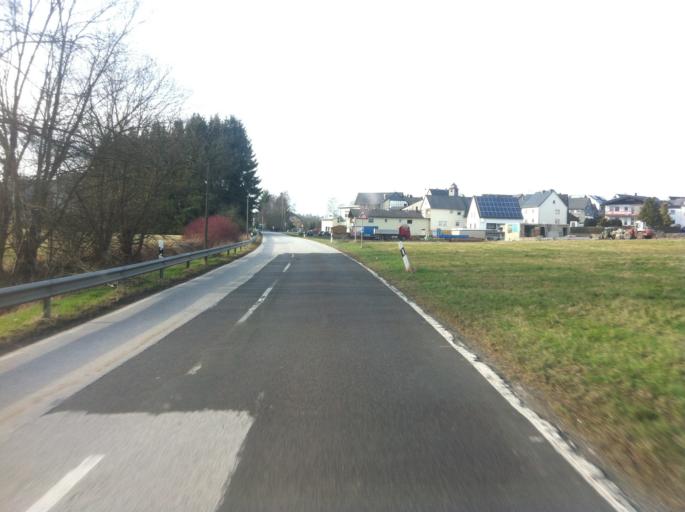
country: DE
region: Rheinland-Pfalz
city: Barenbach
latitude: 49.9445
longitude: 7.3037
